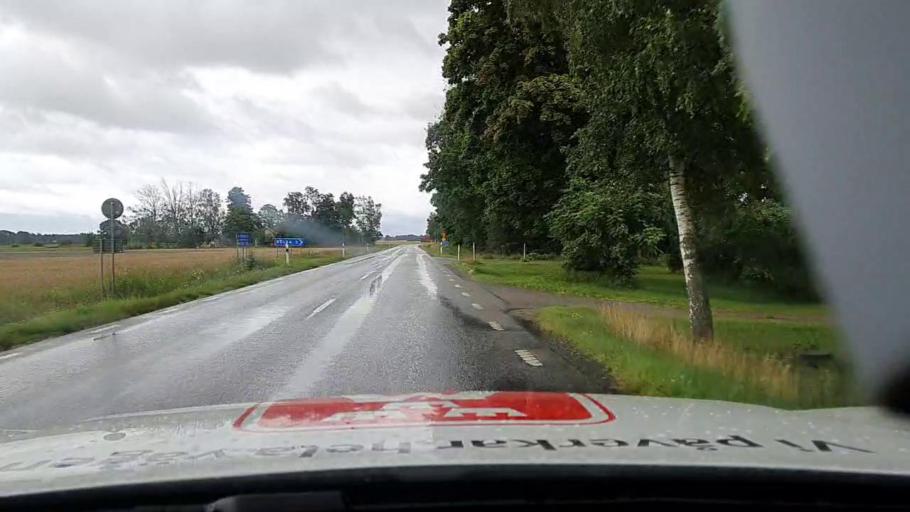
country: SE
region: Vaestra Goetaland
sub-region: Toreboda Kommun
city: Toereboda
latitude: 58.6238
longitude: 14.0137
